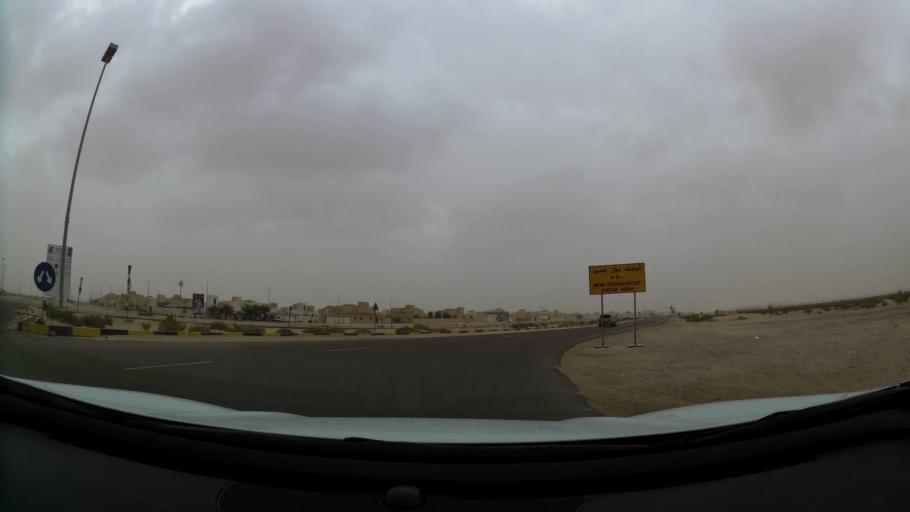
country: AE
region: Abu Dhabi
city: Abu Dhabi
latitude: 24.4607
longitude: 54.7070
